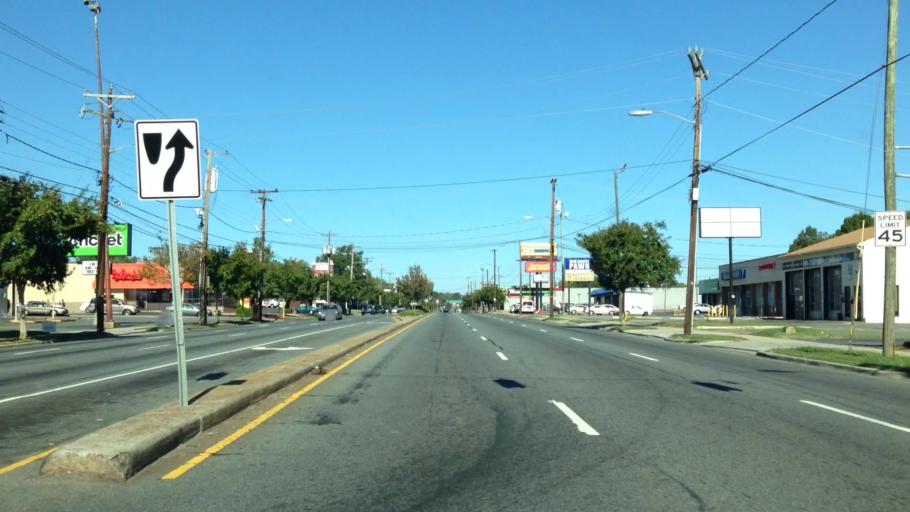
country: US
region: North Carolina
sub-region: Mecklenburg County
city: Charlotte
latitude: 35.2399
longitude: -80.8858
